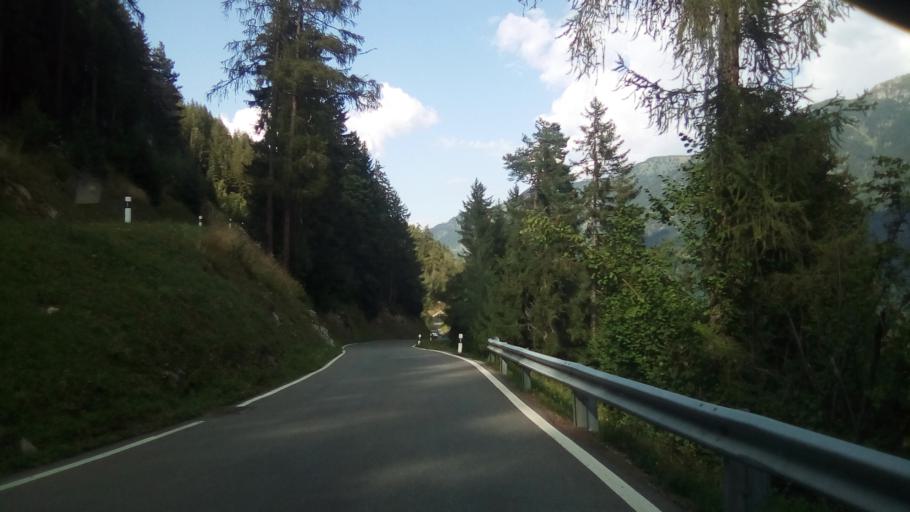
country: CH
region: Valais
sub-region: Entremont District
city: Orsieres
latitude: 46.0250
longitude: 7.1267
